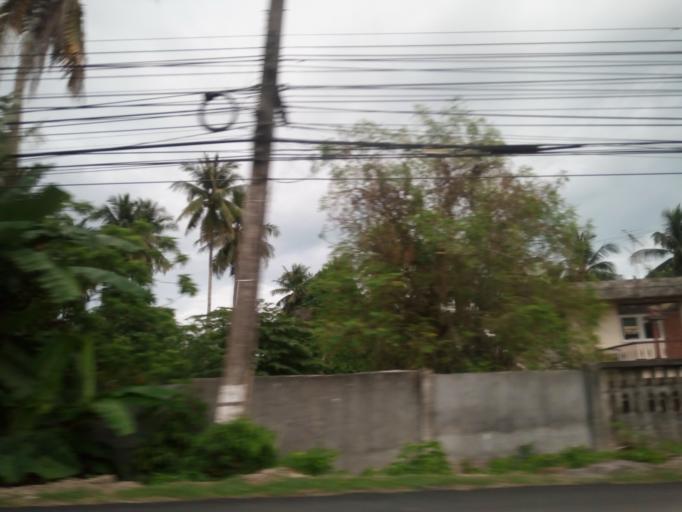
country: TH
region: Phuket
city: Thalang
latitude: 8.1083
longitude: 98.3354
